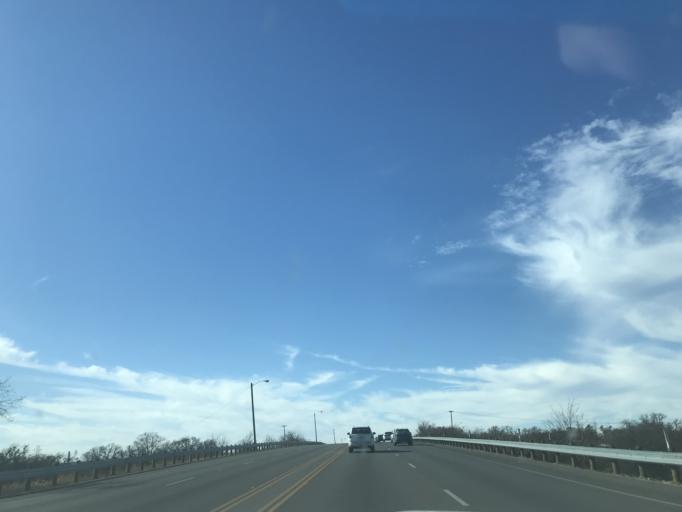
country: US
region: Texas
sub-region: Erath County
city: Stephenville
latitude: 32.2052
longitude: -98.2167
